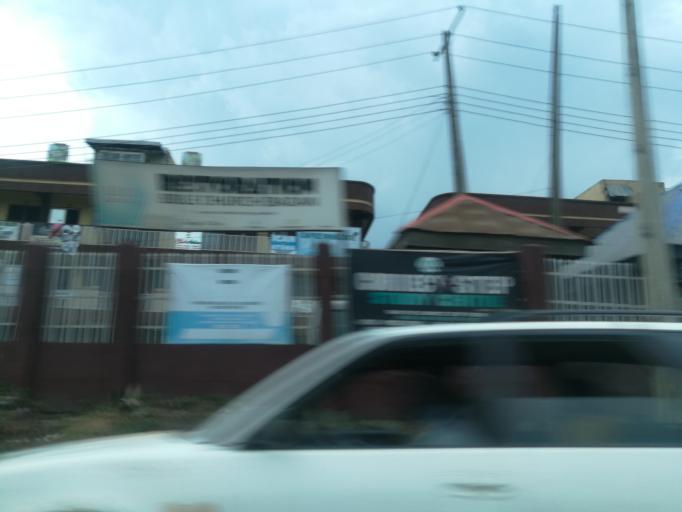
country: NG
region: Oyo
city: Moniya
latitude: 7.4560
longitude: 3.9076
